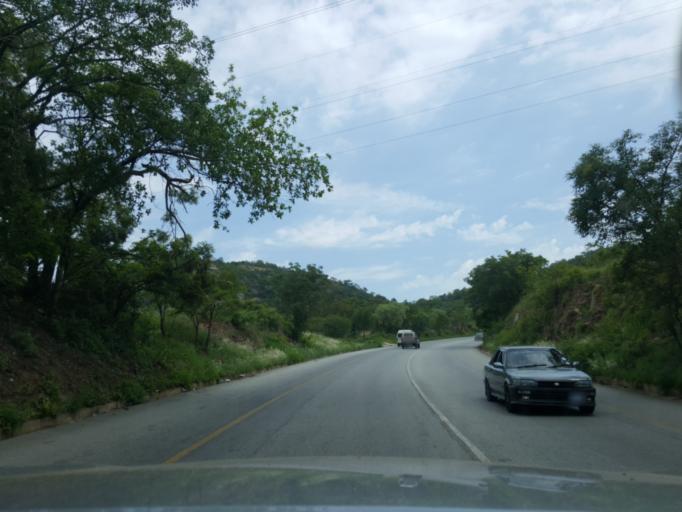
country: ZA
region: Mpumalanga
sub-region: Ehlanzeni District
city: Nelspruit
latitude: -25.4621
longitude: 31.0920
